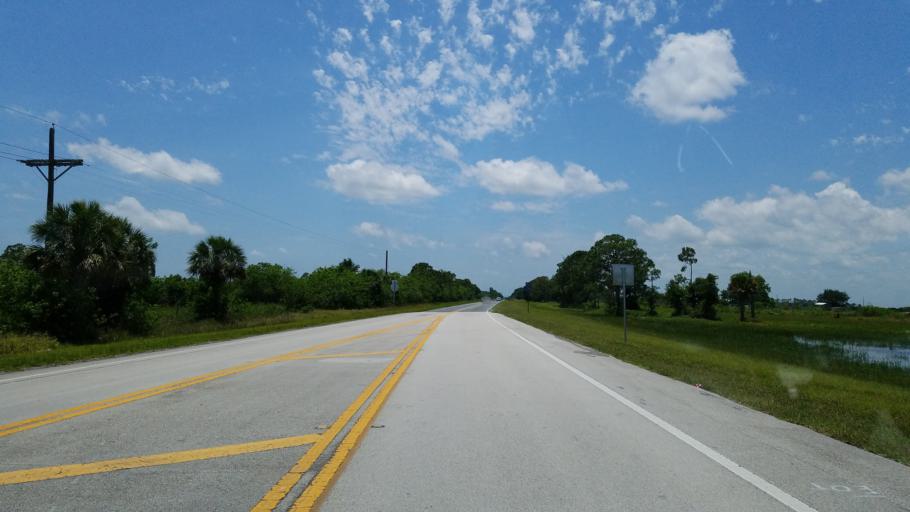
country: US
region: Florida
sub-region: Martin County
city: Palm City
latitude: 27.1617
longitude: -80.4005
